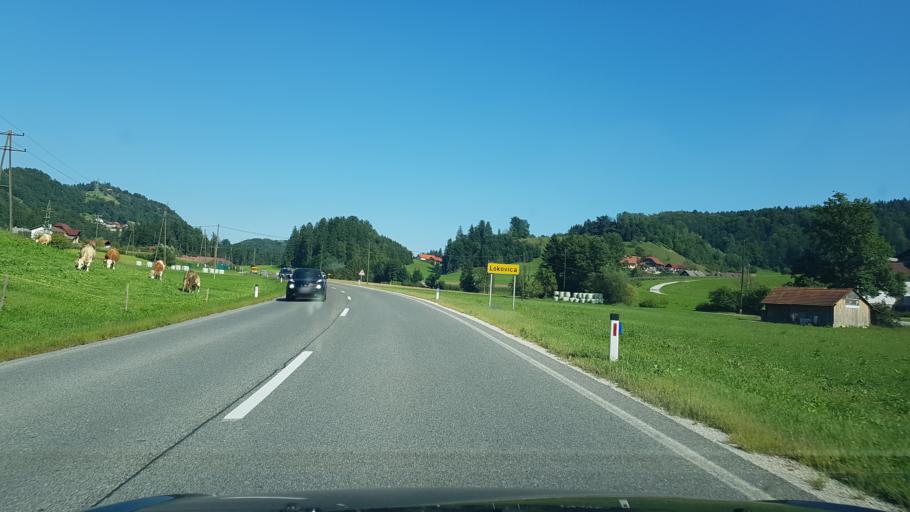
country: SI
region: Sostanj
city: Sostanj
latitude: 46.3611
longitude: 15.0352
